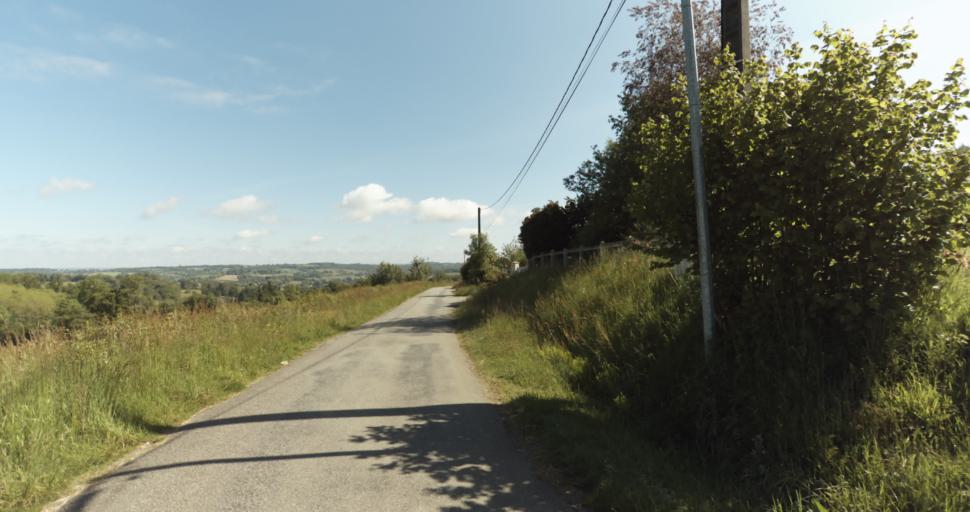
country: FR
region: Limousin
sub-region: Departement de la Haute-Vienne
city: Le Vigen
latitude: 45.7329
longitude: 1.2823
